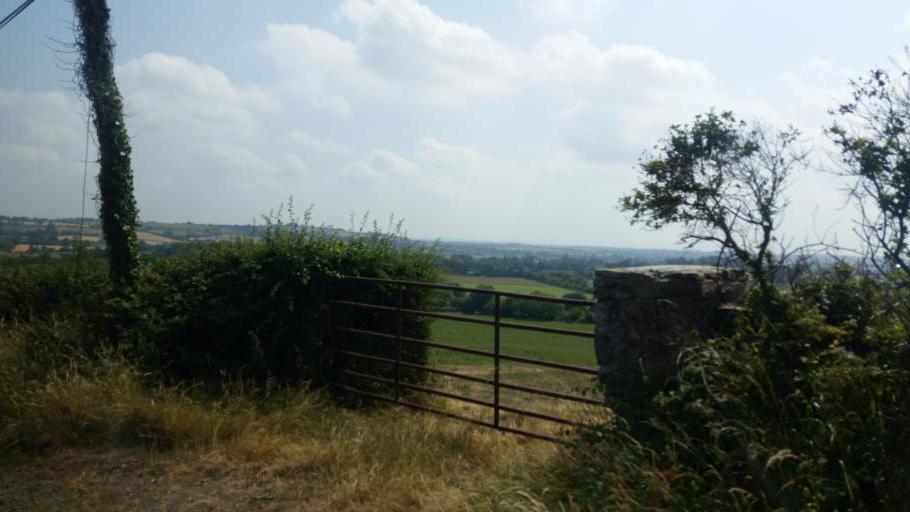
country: IE
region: Leinster
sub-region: An Mhi
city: Stamullin
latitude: 53.5942
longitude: -6.3212
